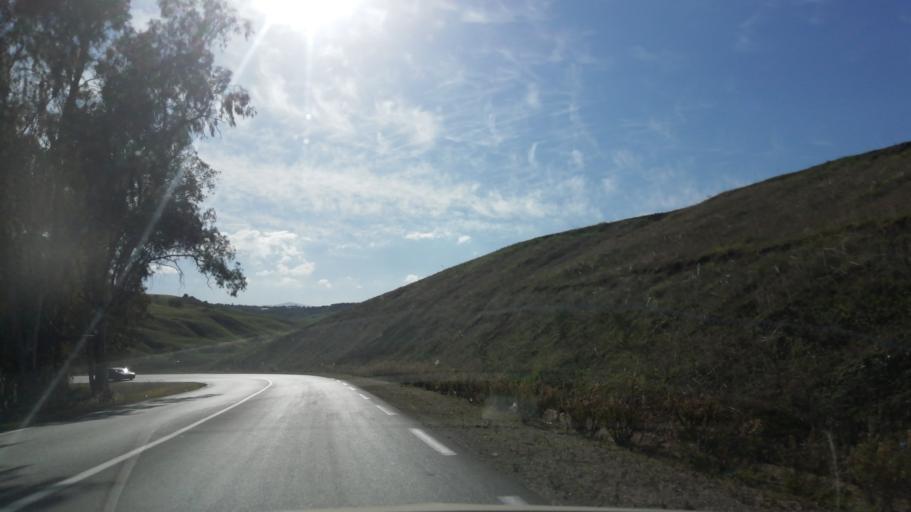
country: DZ
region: Tlemcen
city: Chetouane
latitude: 34.9754
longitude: -1.2392
